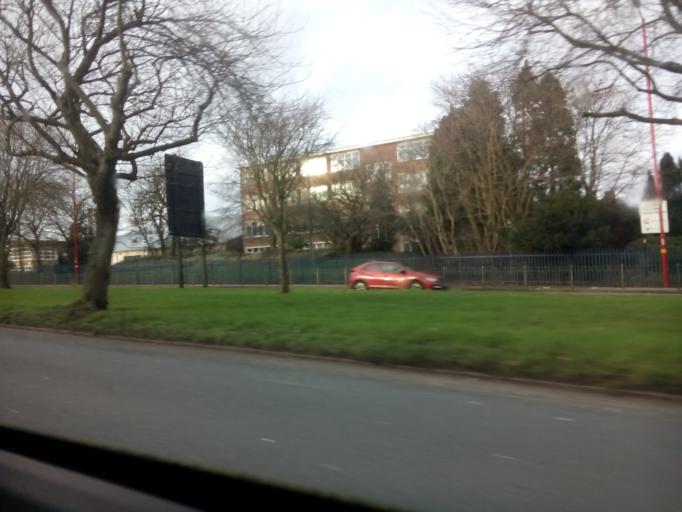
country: GB
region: England
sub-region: Worcestershire
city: Barnt Green
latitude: 52.3955
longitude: -2.0010
